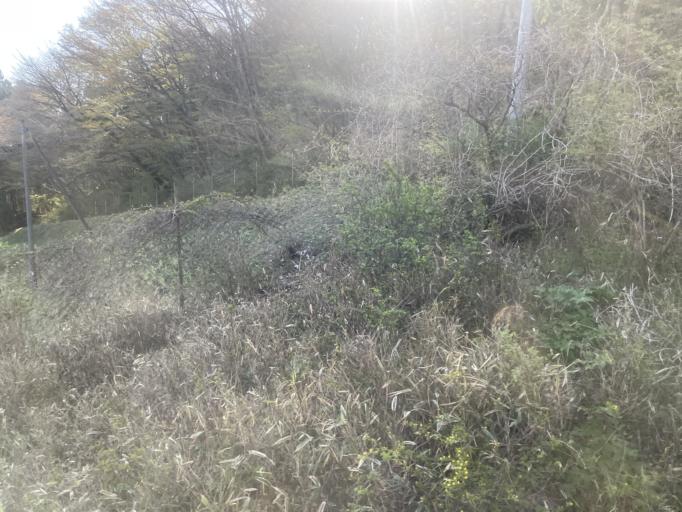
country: JP
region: Iwate
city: Ofunato
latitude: 39.0736
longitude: 141.8166
